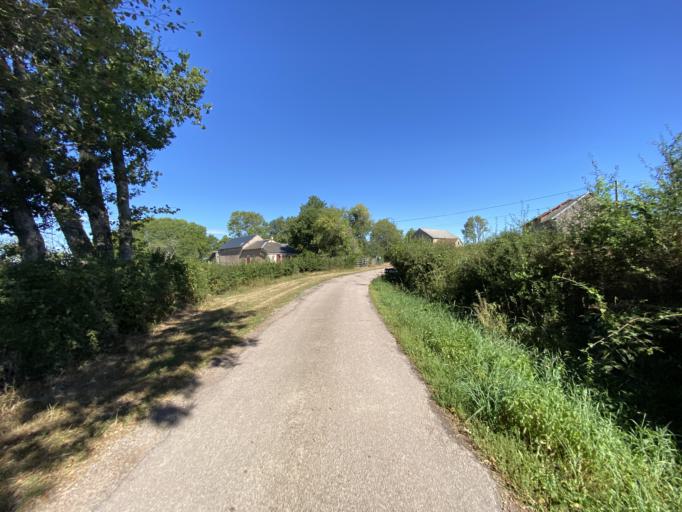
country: FR
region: Bourgogne
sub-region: Departement de la Cote-d'Or
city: Saulieu
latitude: 47.2815
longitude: 4.1806
